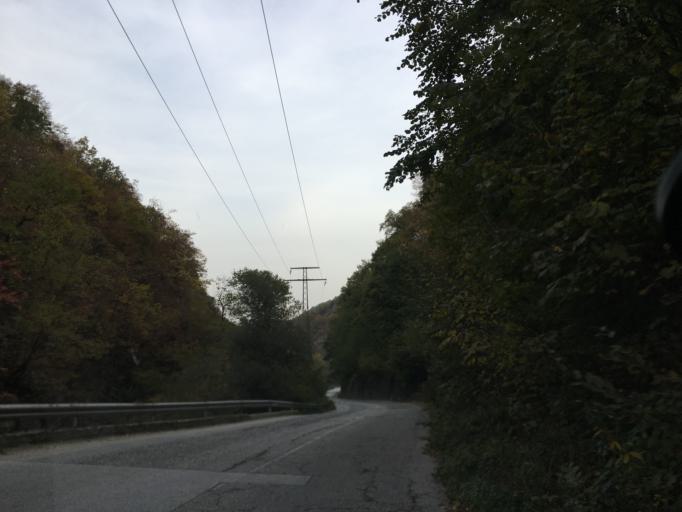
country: BG
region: Pazardzhik
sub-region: Obshtina Belovo
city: Belovo
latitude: 42.1696
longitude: 23.9763
